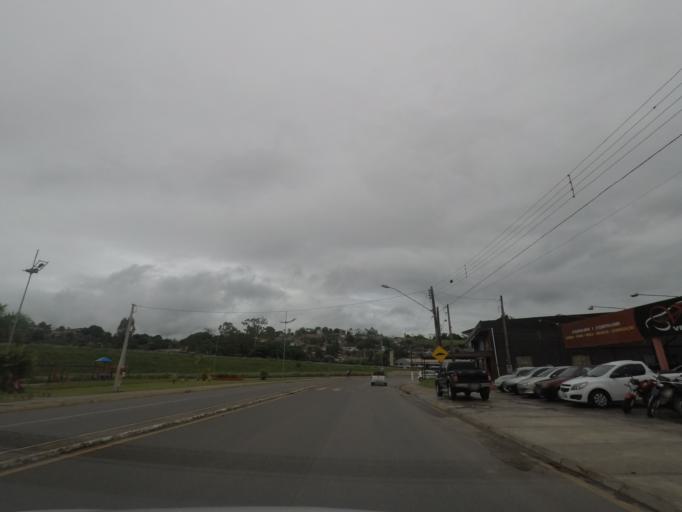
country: BR
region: Sao Paulo
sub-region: Cajati
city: Cajati
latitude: -24.7302
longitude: -48.0995
